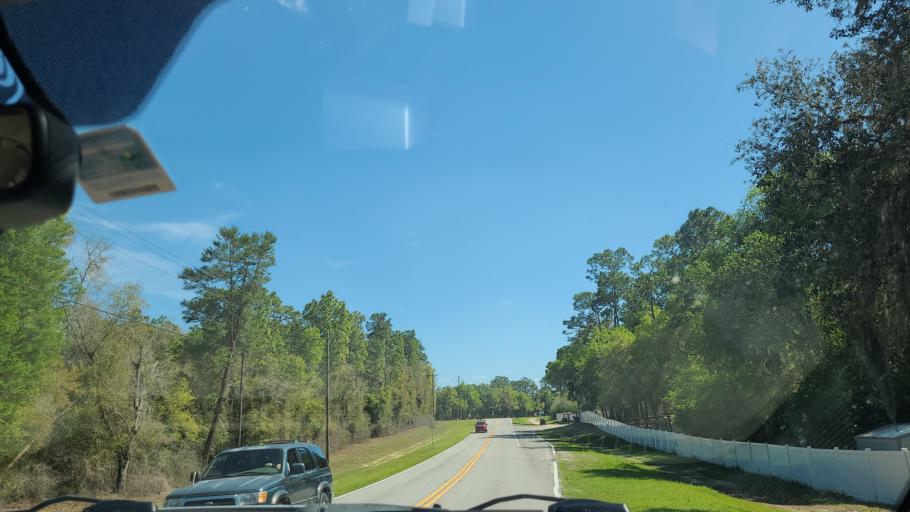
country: US
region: Florida
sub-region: Putnam County
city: Crescent City
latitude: 29.3616
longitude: -81.7372
